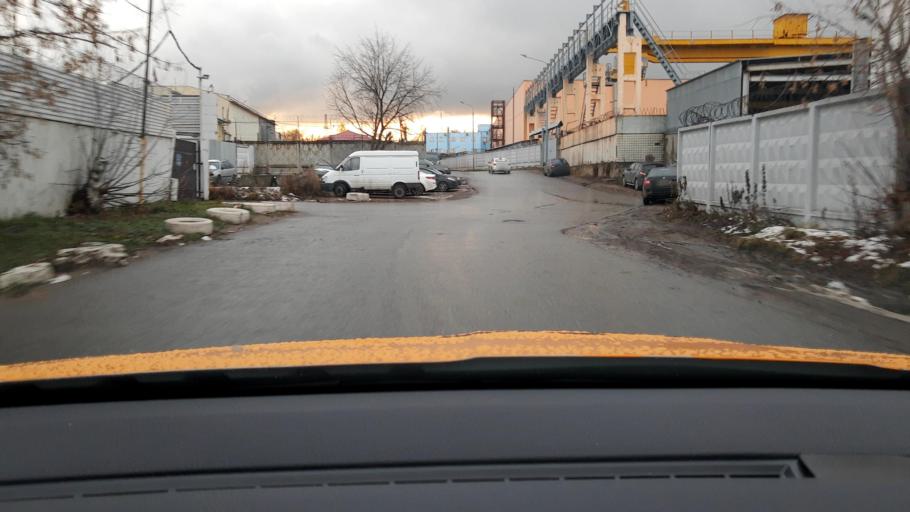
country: RU
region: Moscow
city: Kapotnya
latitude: 55.6625
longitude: 37.8014
